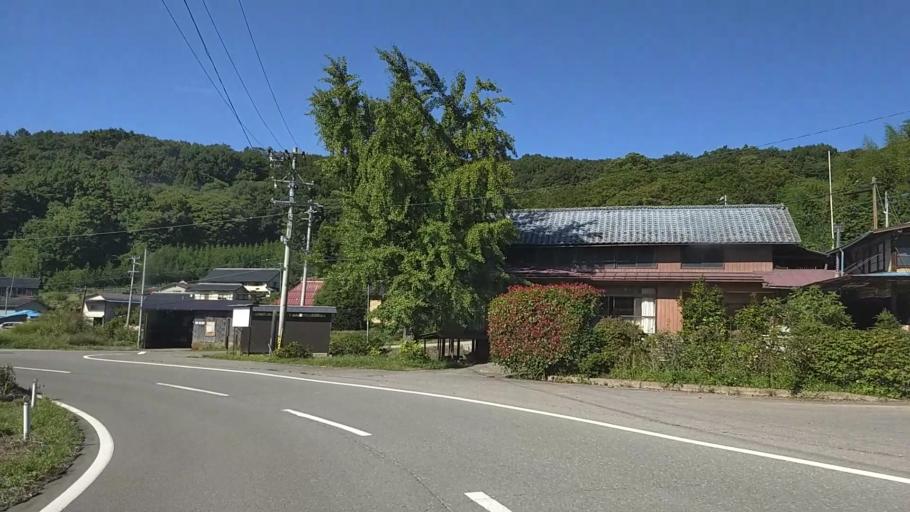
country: JP
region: Nagano
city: Nagano-shi
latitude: 36.6050
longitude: 138.0942
